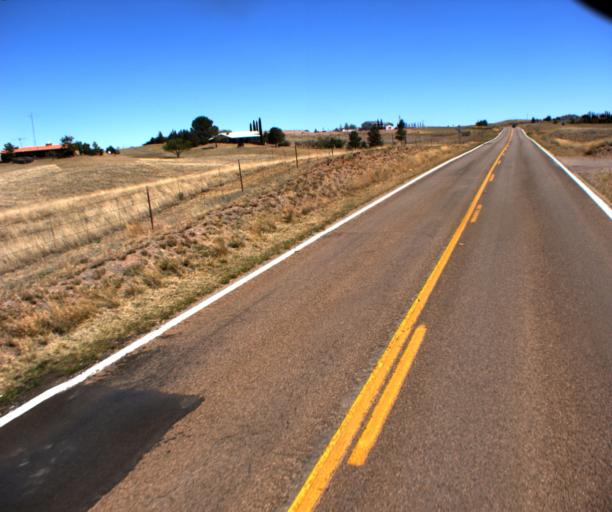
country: US
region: Arizona
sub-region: Cochise County
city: Huachuca City
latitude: 31.6722
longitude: -110.6101
